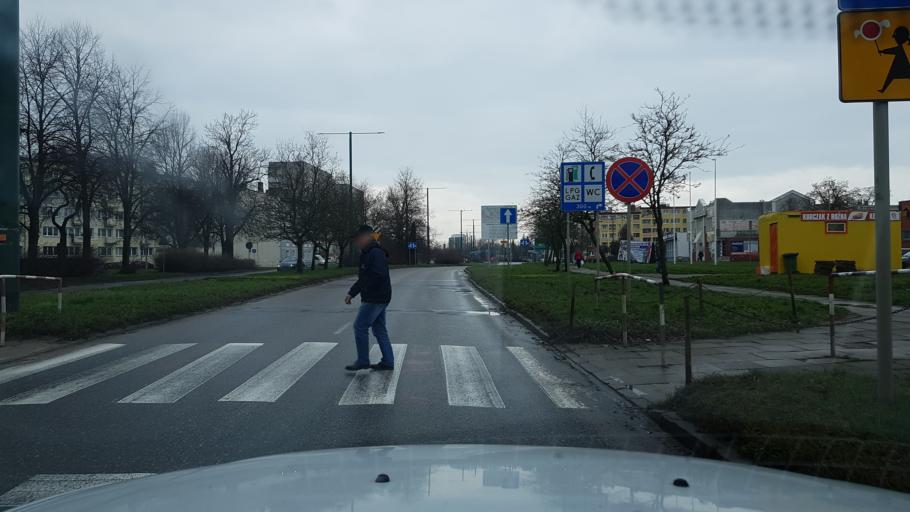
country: PL
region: West Pomeranian Voivodeship
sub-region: Powiat kolobrzeski
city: Kolobrzeg
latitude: 54.1742
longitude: 15.5885
